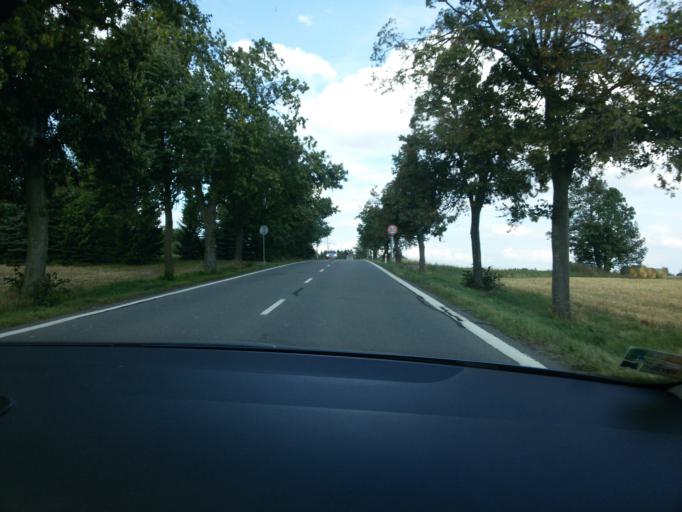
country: CZ
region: Pardubicky
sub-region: Okres Svitavy
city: Policka
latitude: 49.7415
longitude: 16.1815
